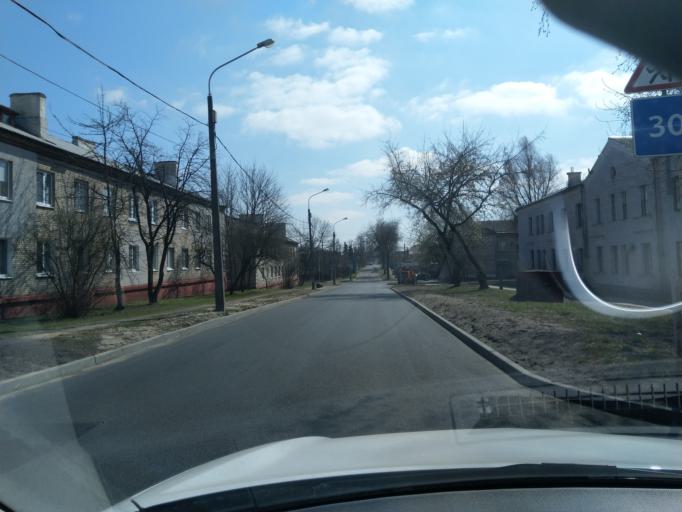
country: BY
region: Minsk
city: Syenitsa
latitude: 53.8709
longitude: 27.5125
